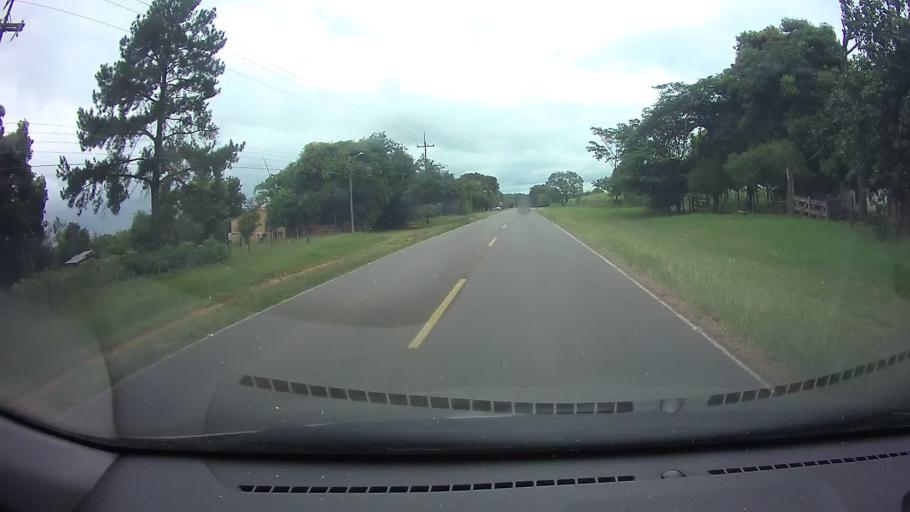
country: PY
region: Central
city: Nueva Italia
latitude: -25.5846
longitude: -57.5067
